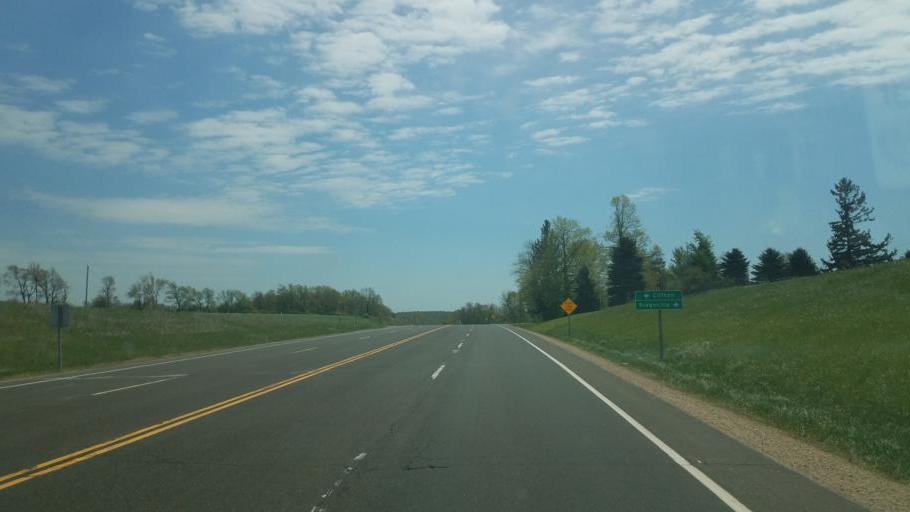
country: US
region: Wisconsin
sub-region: Monroe County
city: Tomah
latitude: 43.8991
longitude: -90.4906
